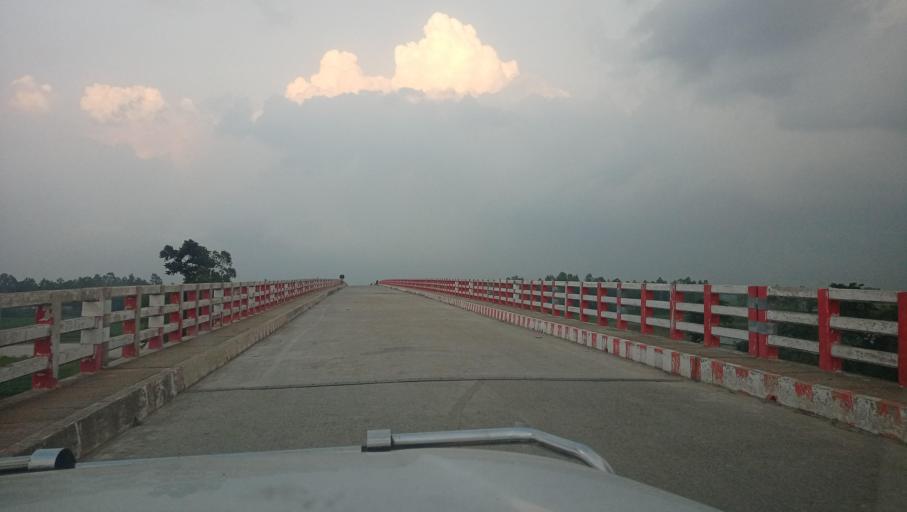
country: BD
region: Dhaka
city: Sherpur
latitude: 25.1768
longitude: 89.7898
